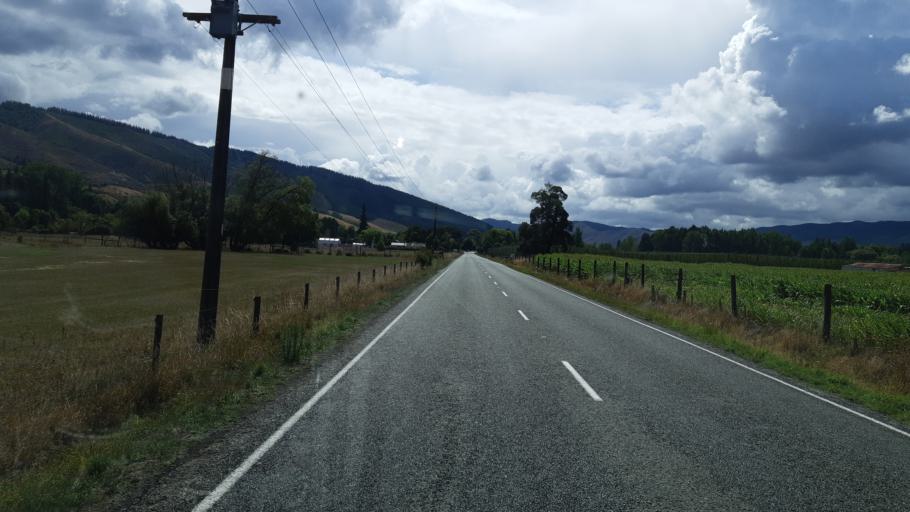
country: NZ
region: Tasman
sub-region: Tasman District
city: Wakefield
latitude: -41.4647
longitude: 172.8091
